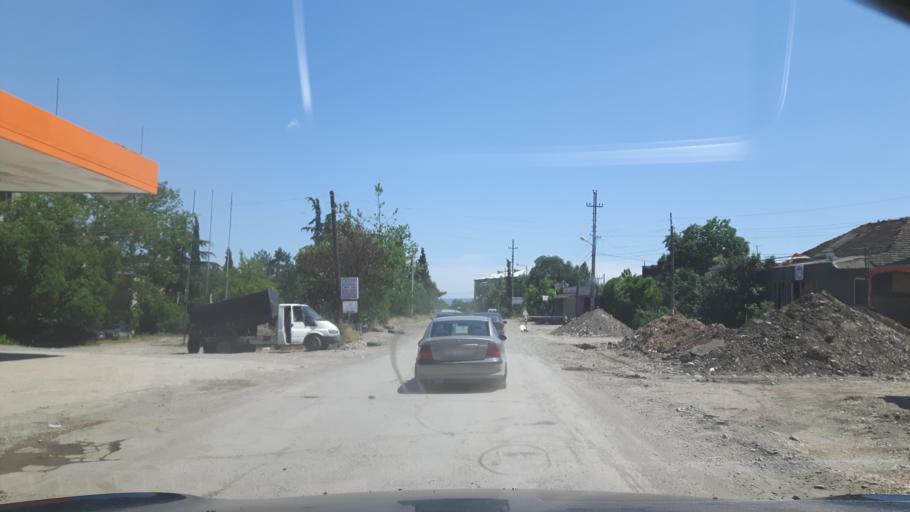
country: GE
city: Tsnori
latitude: 41.6182
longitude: 45.9837
